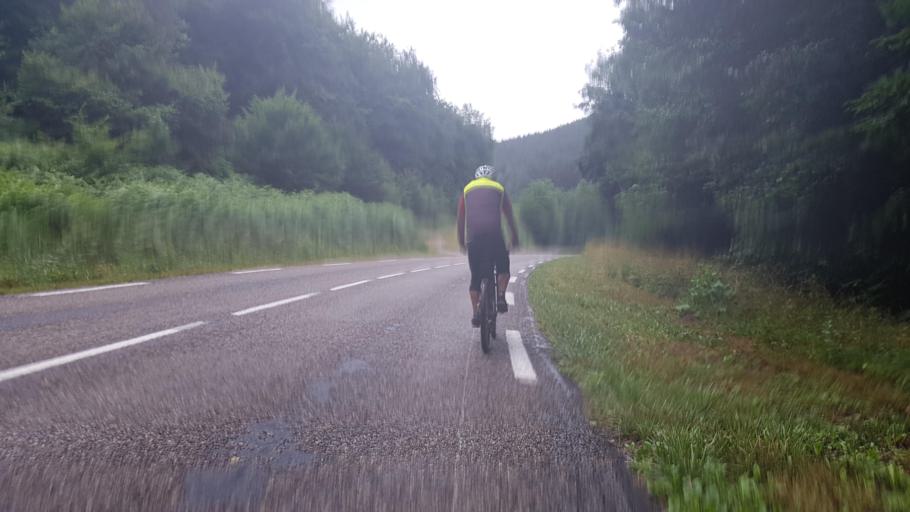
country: FR
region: Alsace
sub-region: Departement du Bas-Rhin
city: Saverne
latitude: 48.7216
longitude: 7.3055
